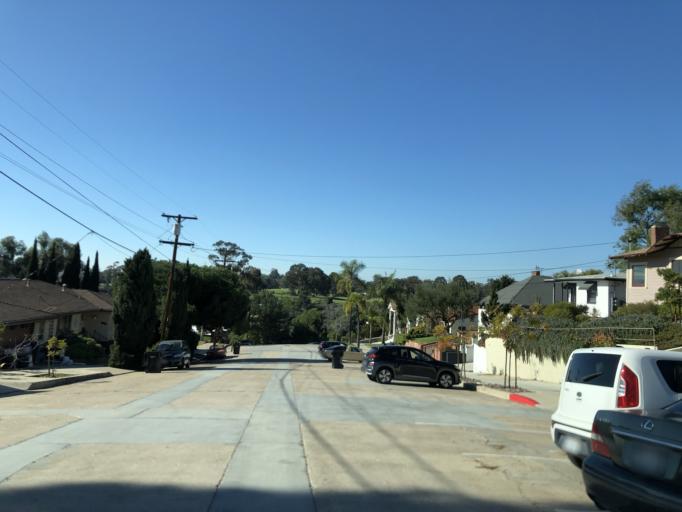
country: US
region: California
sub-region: San Diego County
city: San Diego
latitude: 32.7297
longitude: -117.1321
